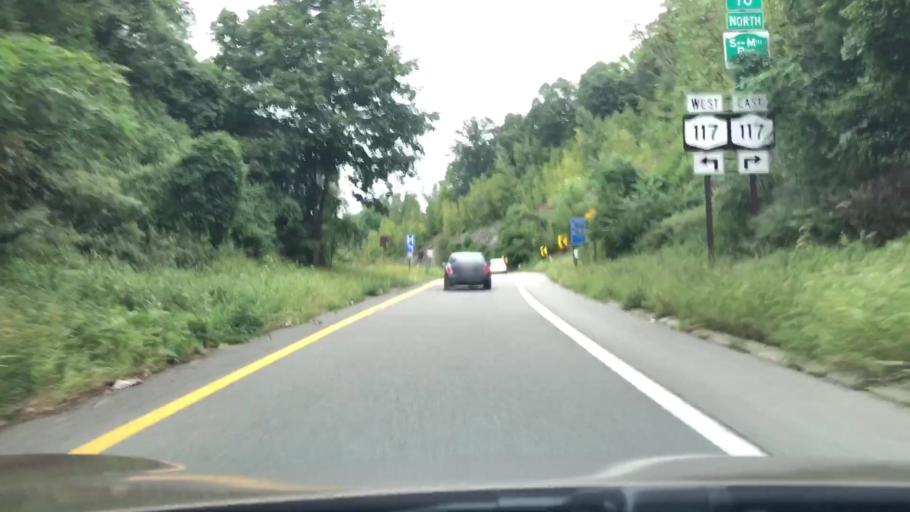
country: US
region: New York
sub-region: Westchester County
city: Pleasantville
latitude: 41.1228
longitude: -73.8066
